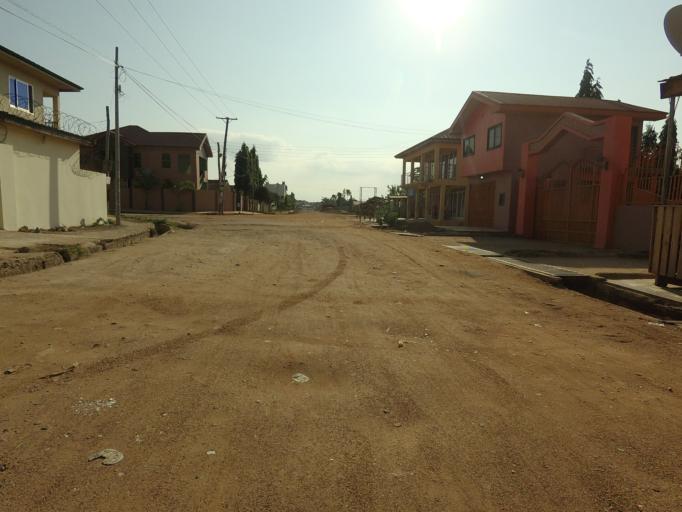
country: GH
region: Greater Accra
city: Nungua
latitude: 5.6363
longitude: -0.0879
